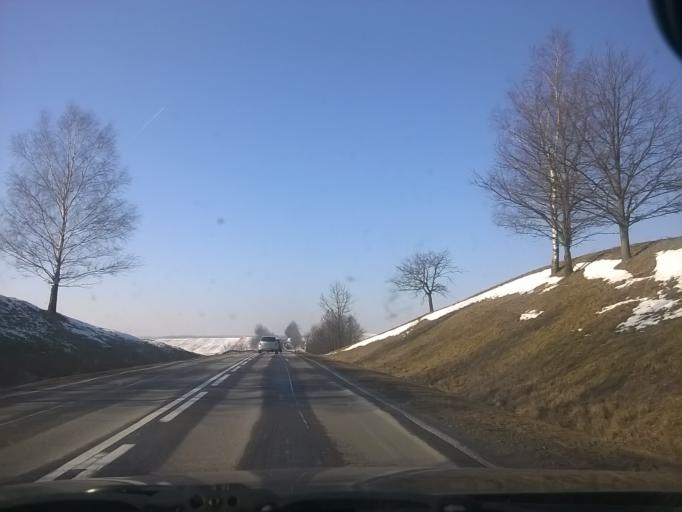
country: PL
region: Warmian-Masurian Voivodeship
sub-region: Powiat mragowski
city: Mragowo
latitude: 53.8411
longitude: 21.1700
